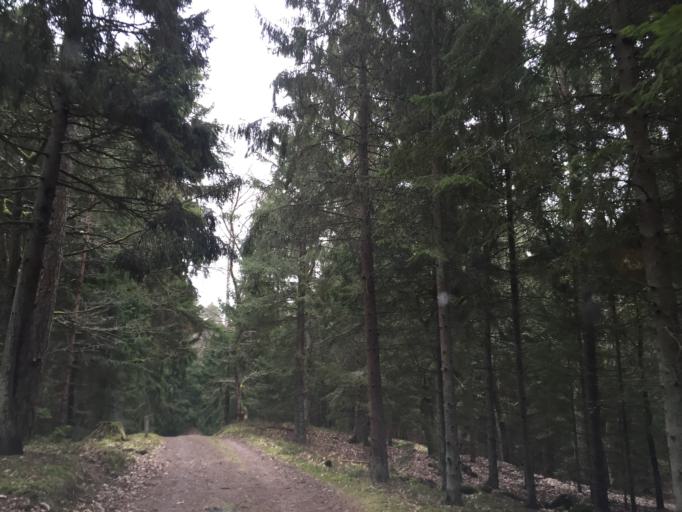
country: LT
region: Klaipedos apskritis
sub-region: Klaipeda
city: Klaipeda
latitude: 55.5553
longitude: 21.1204
